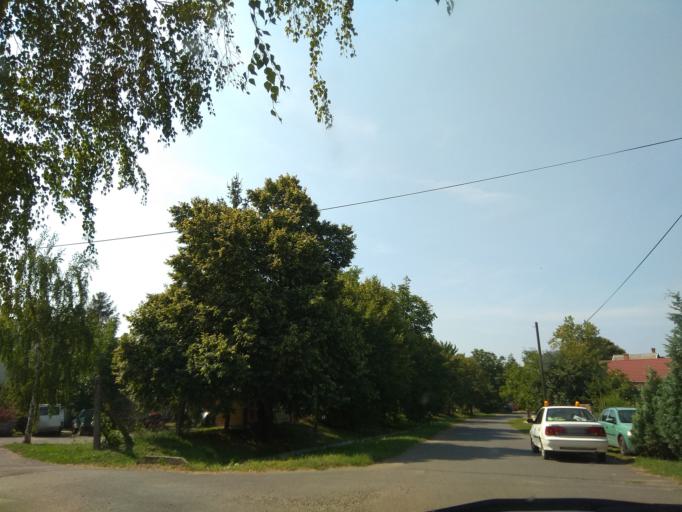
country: HU
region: Borsod-Abauj-Zemplen
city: Tallya
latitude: 48.2332
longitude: 21.2271
